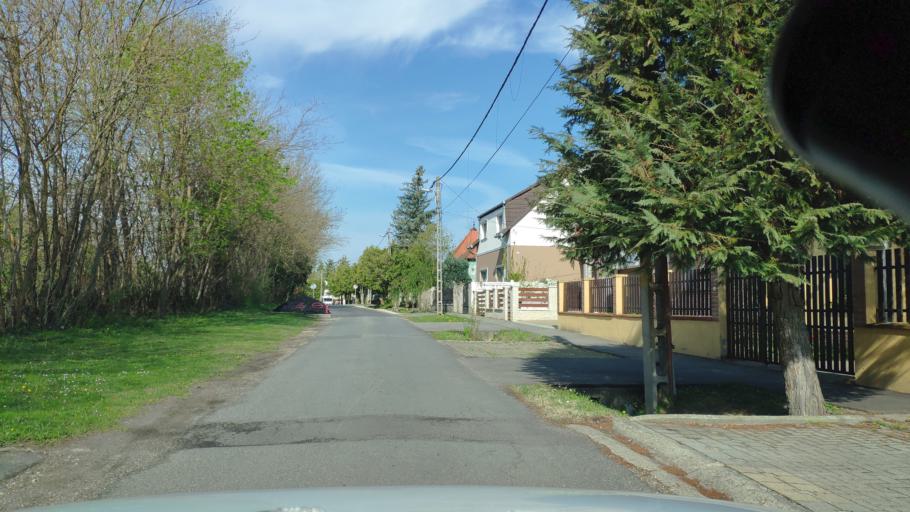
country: HU
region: Zala
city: Nagykanizsa
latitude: 46.4500
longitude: 17.0021
